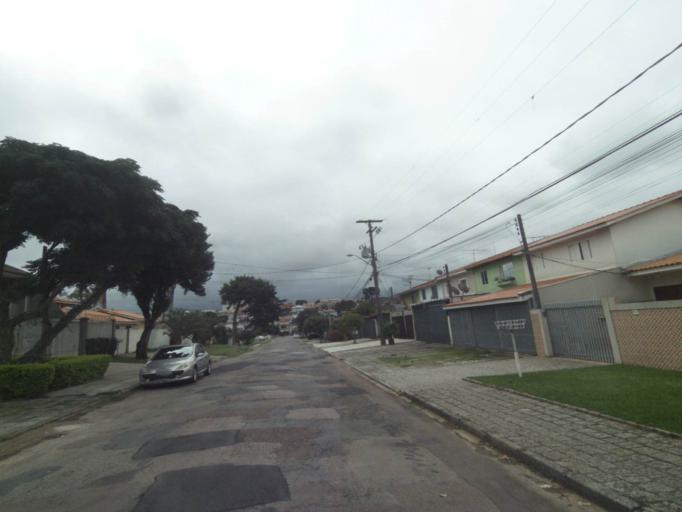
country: BR
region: Parana
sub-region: Curitiba
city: Curitiba
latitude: -25.4875
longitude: -49.2815
